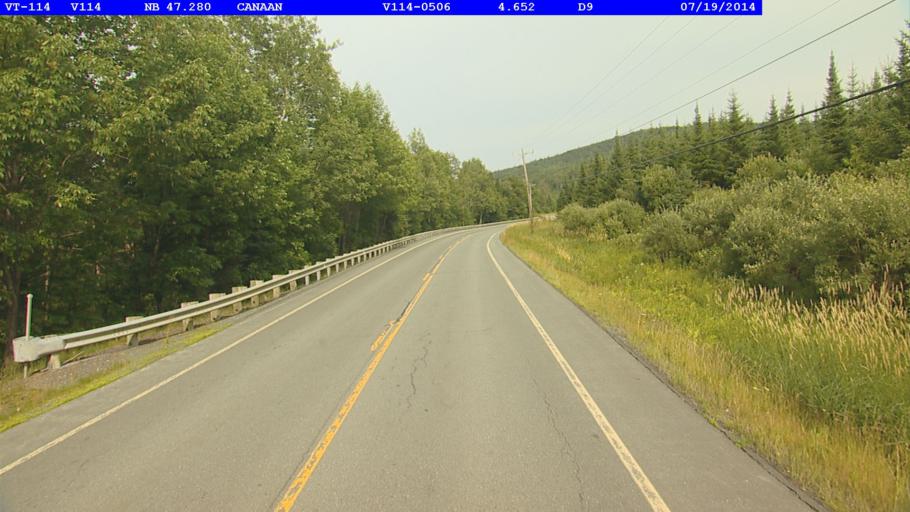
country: US
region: New Hampshire
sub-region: Coos County
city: Colebrook
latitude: 45.0071
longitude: -71.6013
